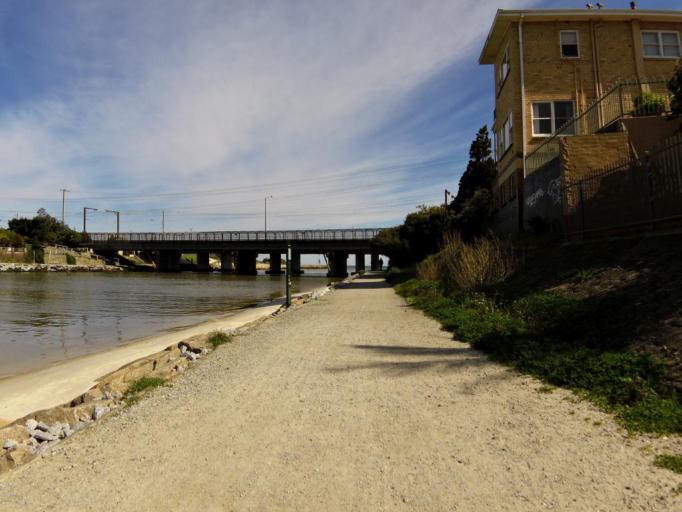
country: AU
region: Victoria
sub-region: Kingston
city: Bonbeach
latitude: -38.0720
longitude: 145.1227
